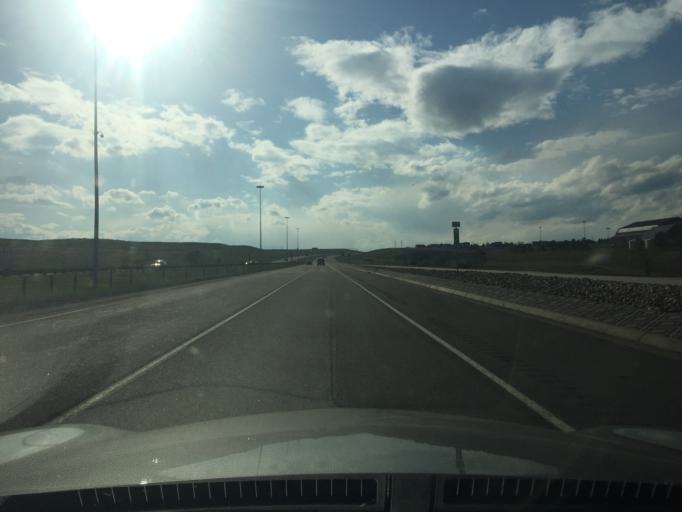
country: US
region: Colorado
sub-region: Adams County
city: Todd Creek
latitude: 39.9537
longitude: -104.8743
